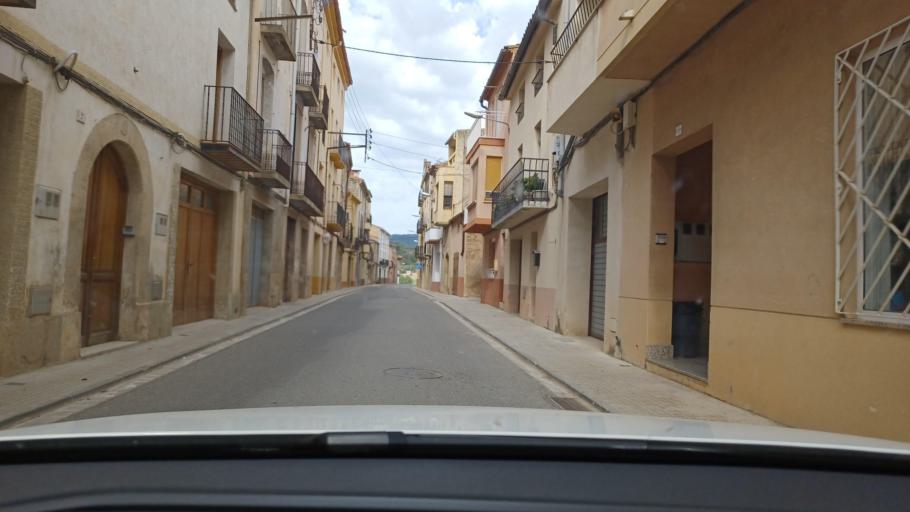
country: ES
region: Catalonia
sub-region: Provincia de Tarragona
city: Bot
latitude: 41.0091
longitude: 0.3842
